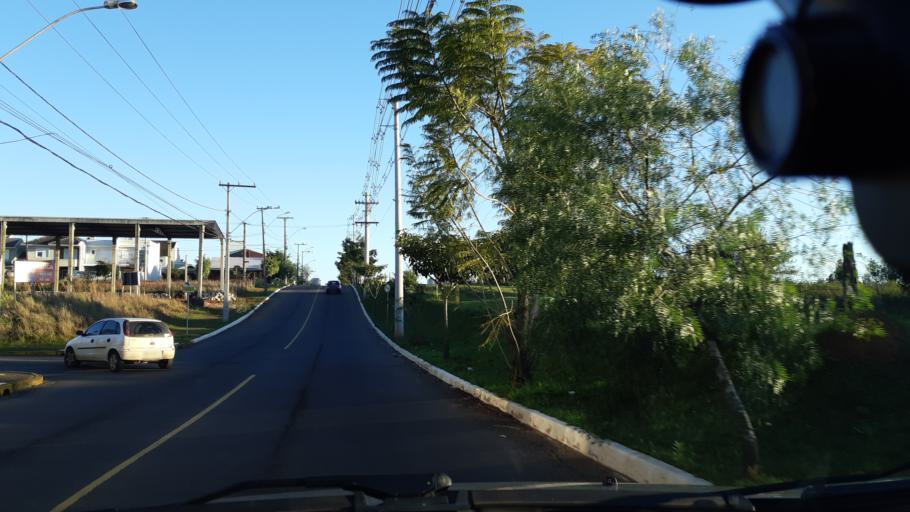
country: BR
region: Rio Grande do Sul
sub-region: Canoas
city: Canoas
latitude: -29.9134
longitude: -51.1542
